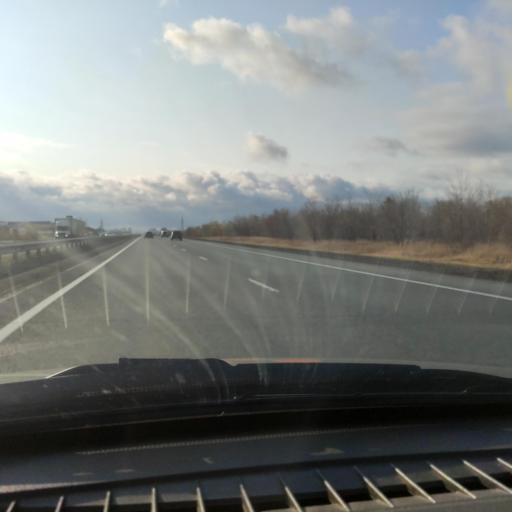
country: RU
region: Samara
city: Tol'yatti
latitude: 53.5670
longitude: 49.3744
